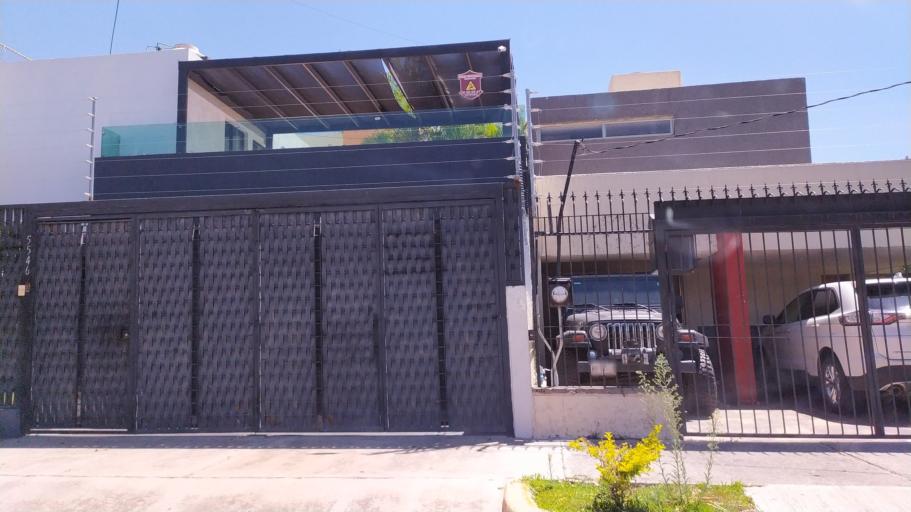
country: MX
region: Jalisco
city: Zapopan2
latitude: 20.6903
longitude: -103.4279
